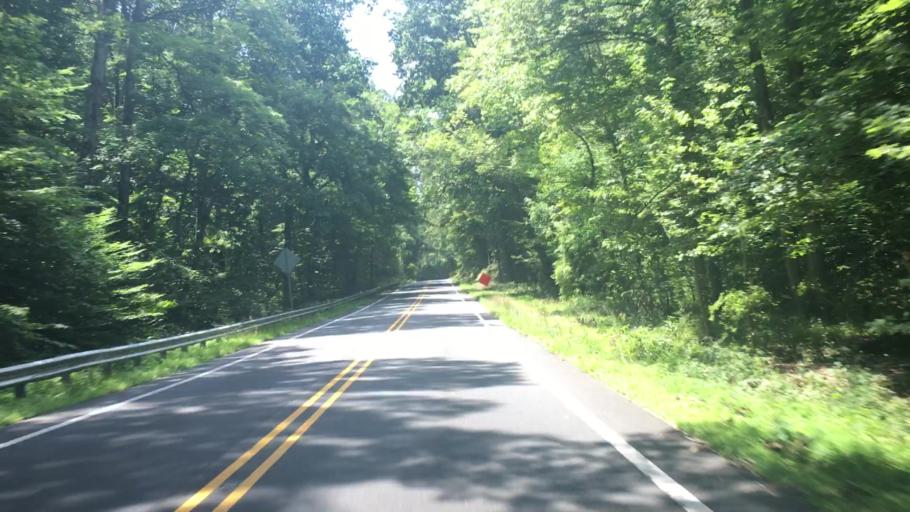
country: US
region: Virginia
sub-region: King George County
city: Passapatanzy
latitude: 38.3012
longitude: -77.2919
